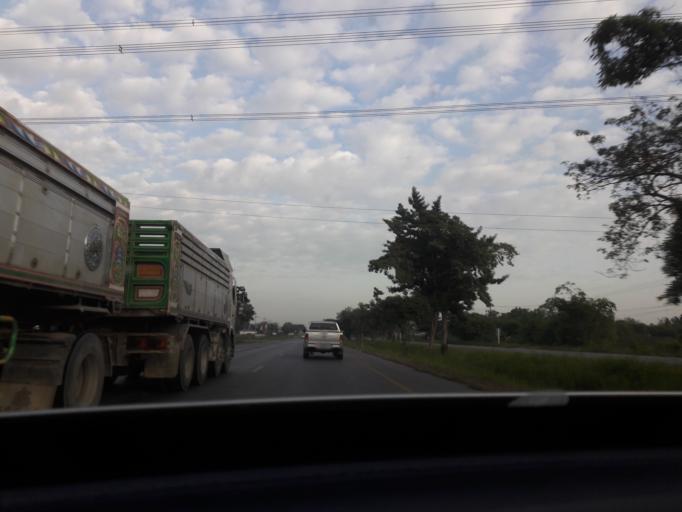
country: TH
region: Phra Nakhon Si Ayutthaya
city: Bang Pa-in
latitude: 14.2693
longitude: 100.5313
